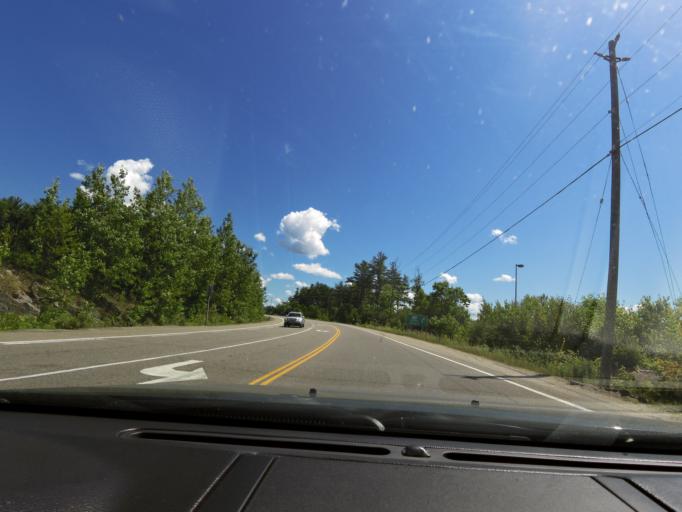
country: CA
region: Ontario
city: Bracebridge
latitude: 45.0505
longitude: -79.2928
